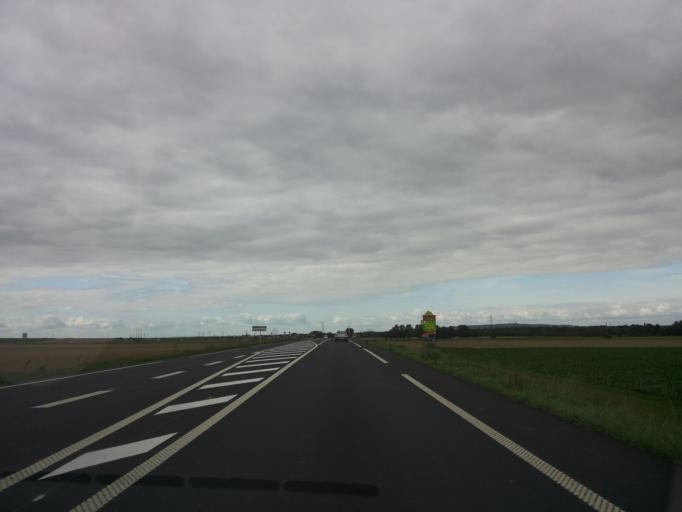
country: FR
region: Champagne-Ardenne
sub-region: Departement de la Marne
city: Verzy
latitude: 49.1574
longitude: 4.2046
